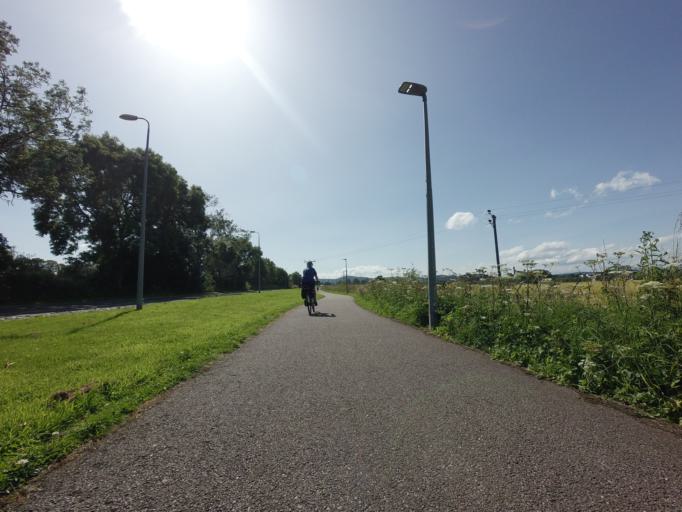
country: GB
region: Scotland
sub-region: Highland
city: Inverness
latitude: 57.4725
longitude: -4.1743
